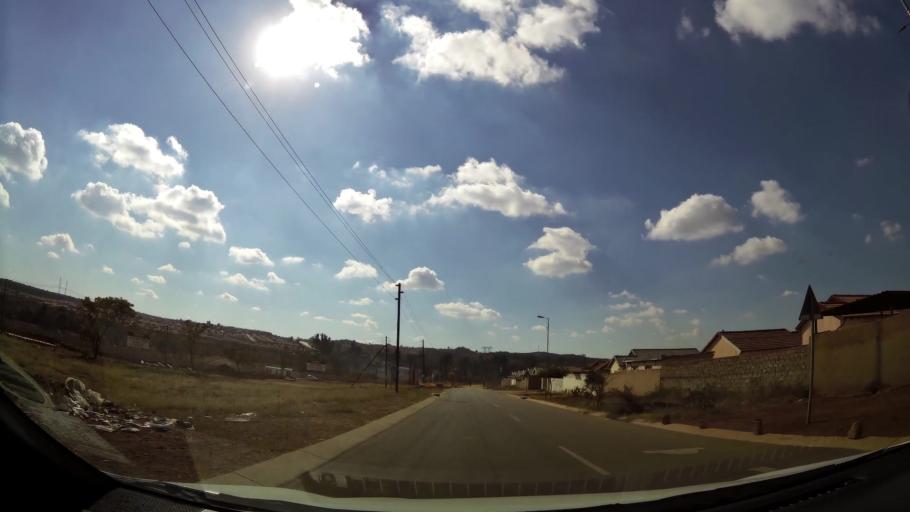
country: ZA
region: Gauteng
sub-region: City of Tshwane Metropolitan Municipality
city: Cullinan
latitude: -25.6872
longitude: 28.4136
